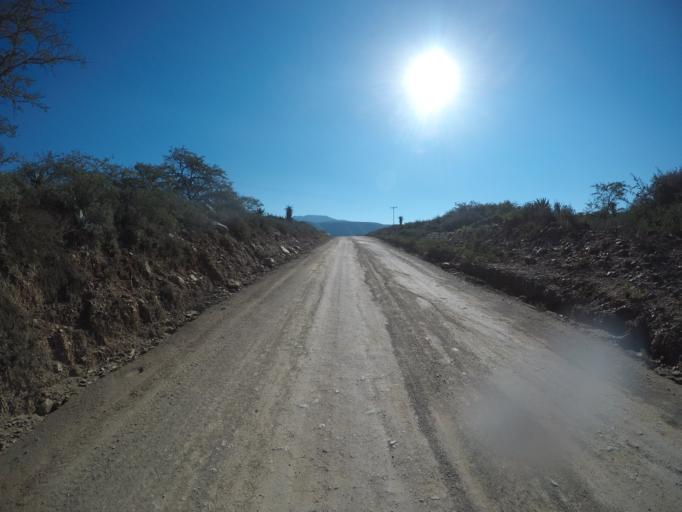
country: ZA
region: Eastern Cape
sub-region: Cacadu District Municipality
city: Kruisfontein
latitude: -33.6727
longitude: 24.5764
